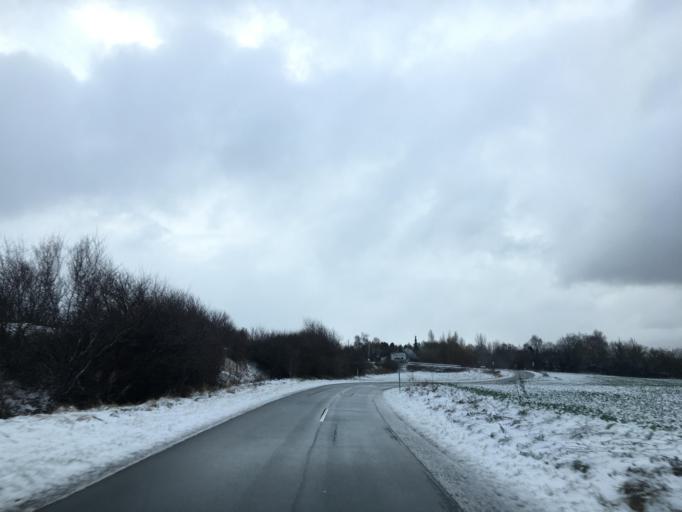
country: DK
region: Zealand
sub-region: Odsherred Kommune
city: Asnaes
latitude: 55.8329
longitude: 11.5636
